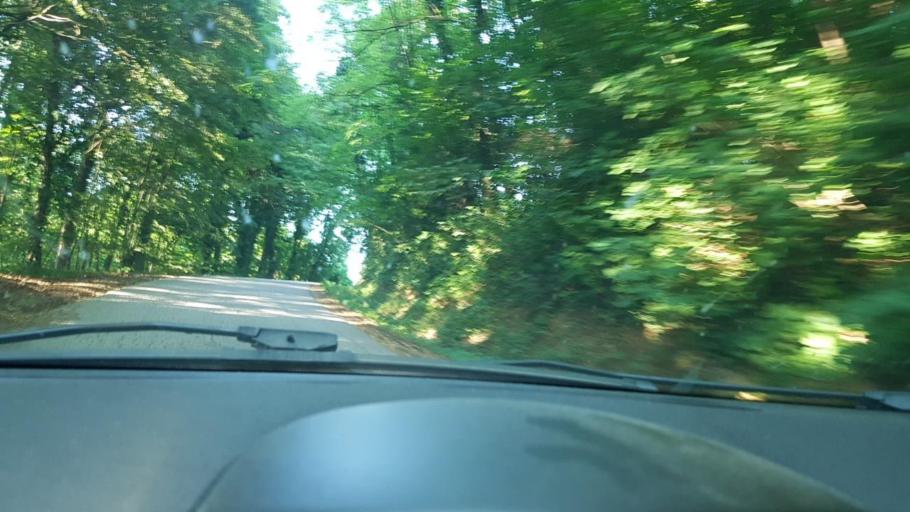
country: HR
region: Krapinsko-Zagorska
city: Mihovljan
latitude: 46.0930
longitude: 15.9468
